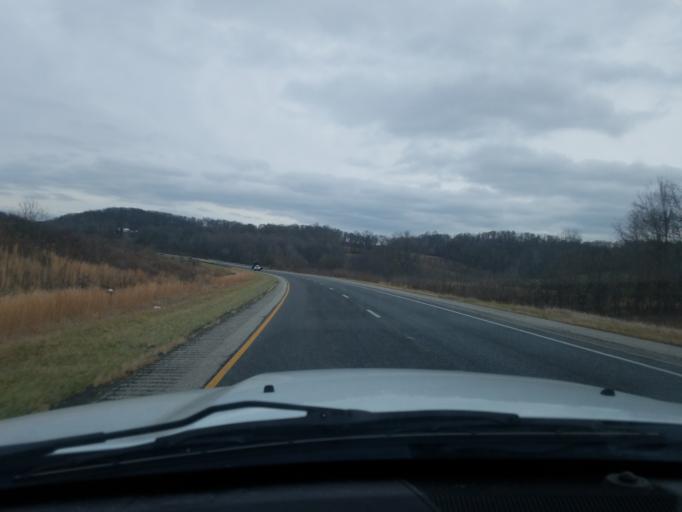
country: US
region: Indiana
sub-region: Dubois County
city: Ferdinand
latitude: 38.2054
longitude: -86.7869
